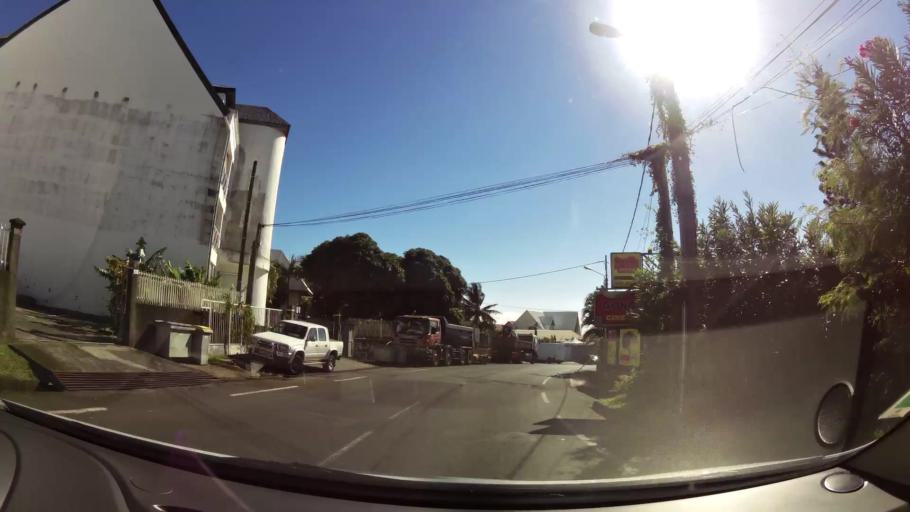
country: RE
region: Reunion
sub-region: Reunion
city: Saint-Denis
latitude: -20.9116
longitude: 55.4850
